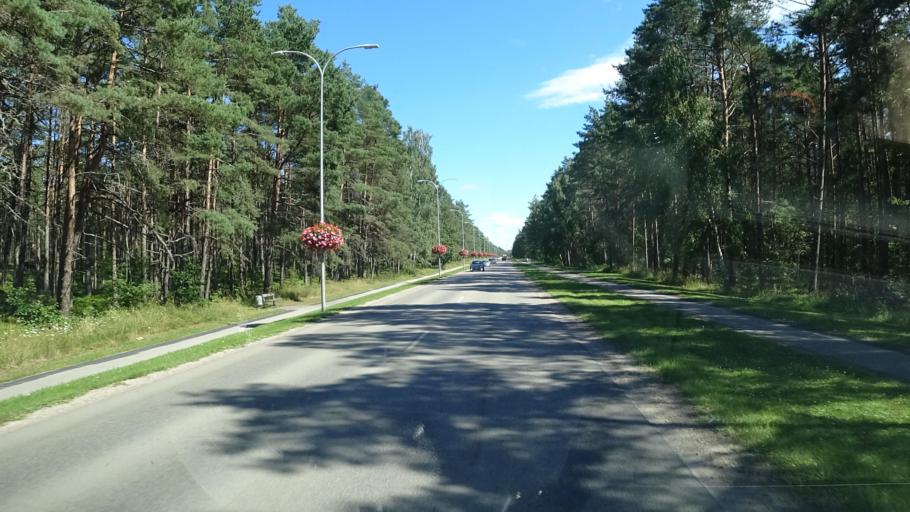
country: LV
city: Tireli
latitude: 56.9671
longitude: 23.5823
